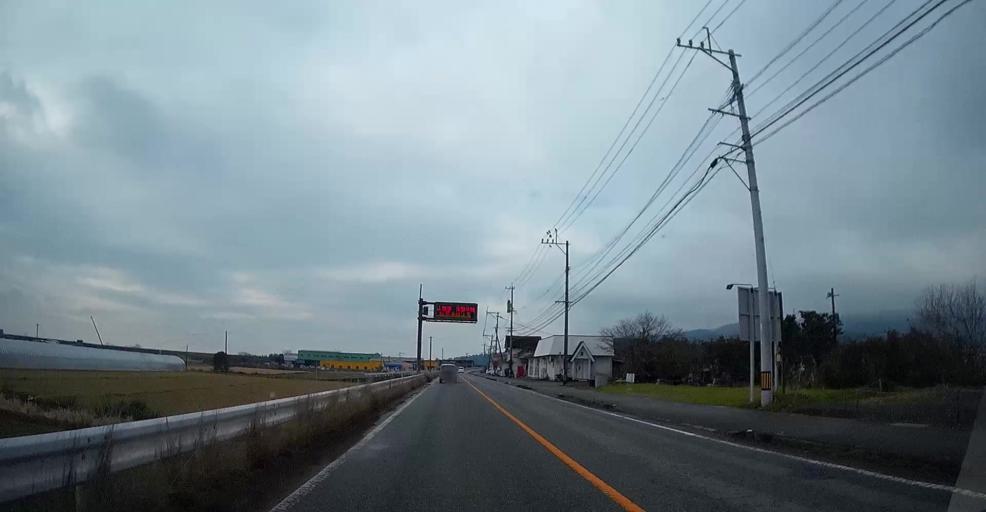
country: JP
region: Kumamoto
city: Matsubase
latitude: 32.6442
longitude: 130.6551
